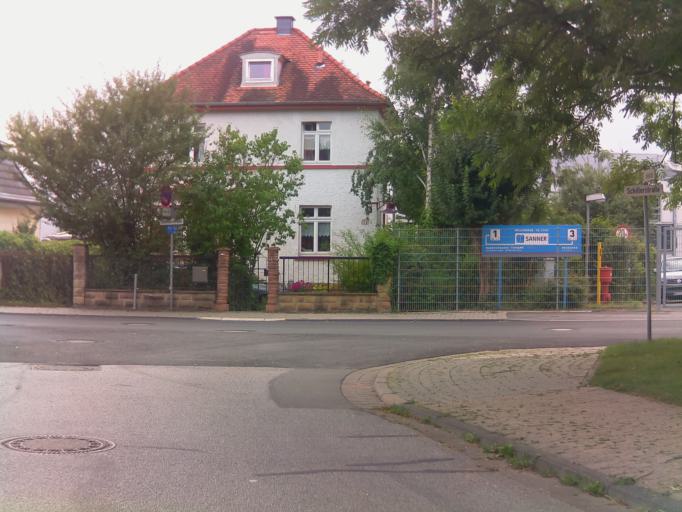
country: DE
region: Hesse
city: Zwingenberg
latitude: 49.7040
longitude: 8.6149
